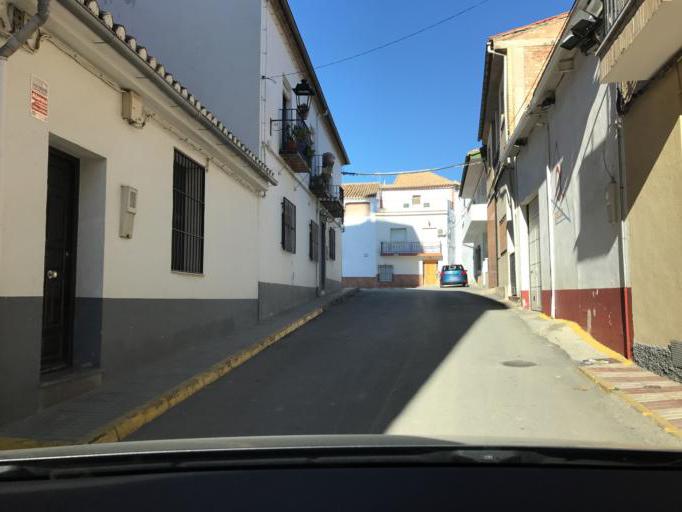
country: ES
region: Andalusia
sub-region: Provincia de Granada
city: Alfacar
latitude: 37.2369
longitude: -3.5700
